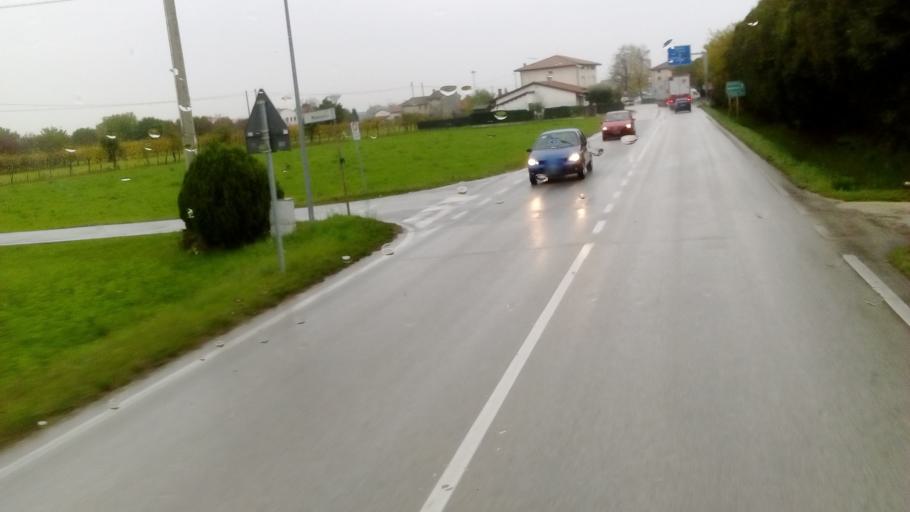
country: IT
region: Veneto
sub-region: Provincia di Vicenza
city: Montecchio Precalcino
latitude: 45.6724
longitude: 11.5729
